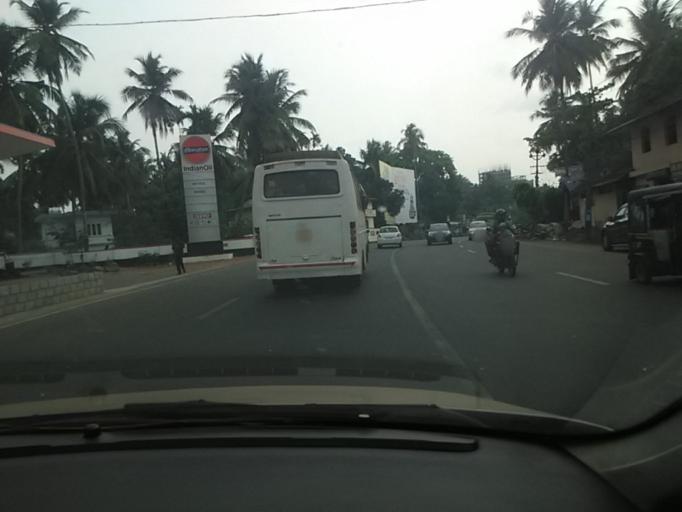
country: IN
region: Kerala
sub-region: Kozhikode
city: Kozhikode
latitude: 11.2774
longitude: 75.7801
